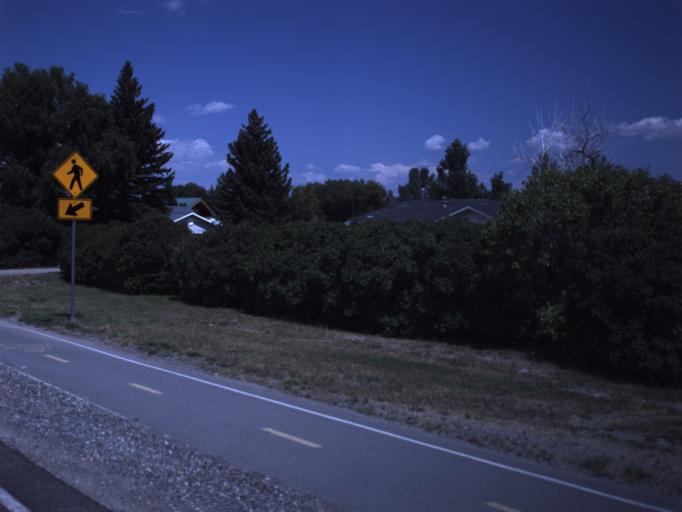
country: US
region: Idaho
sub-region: Bear Lake County
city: Paris
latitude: 41.9112
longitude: -111.3907
